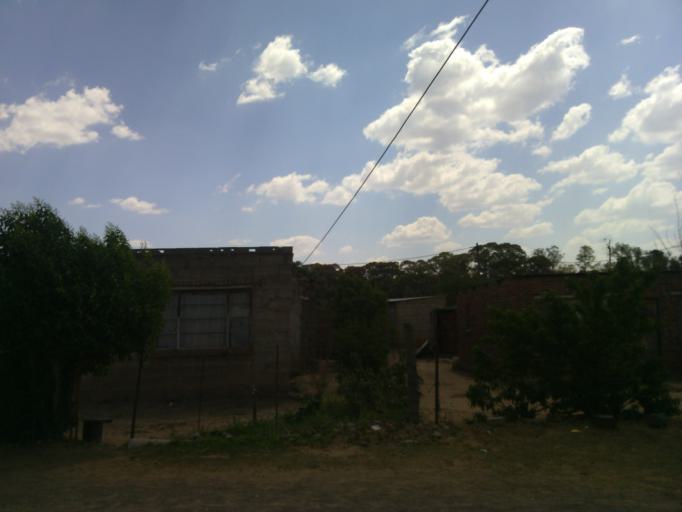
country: ZA
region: Orange Free State
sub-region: Xhariep District Municipality
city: Dewetsdorp
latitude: -29.5773
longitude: 26.6806
